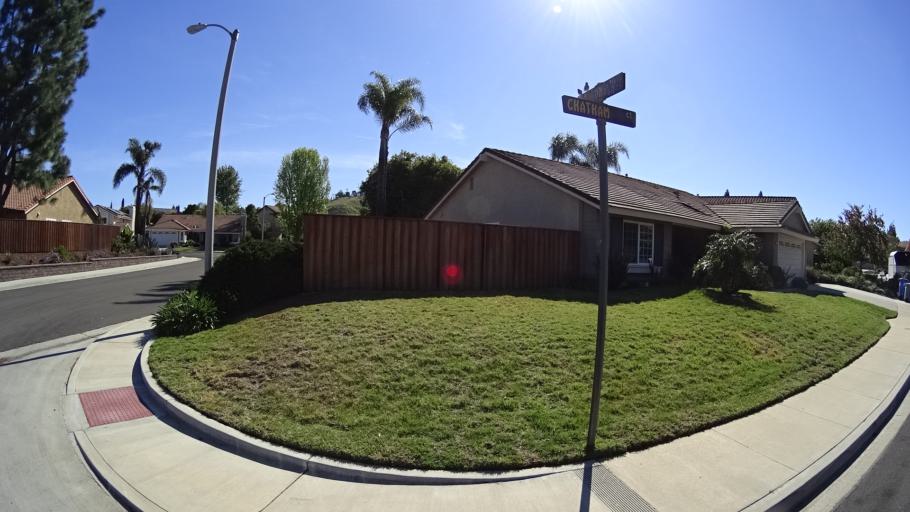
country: US
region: California
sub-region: Ventura County
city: Thousand Oaks
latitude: 34.2266
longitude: -118.8599
